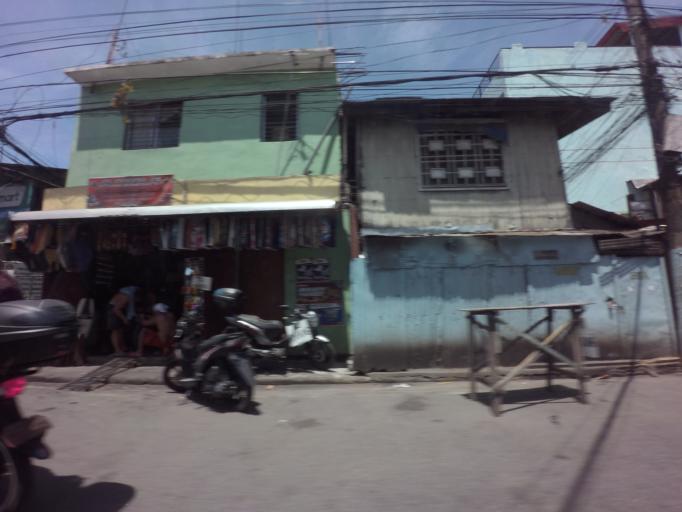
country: PH
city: Sambayanihan People's Village
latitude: 14.5095
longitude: 120.9948
